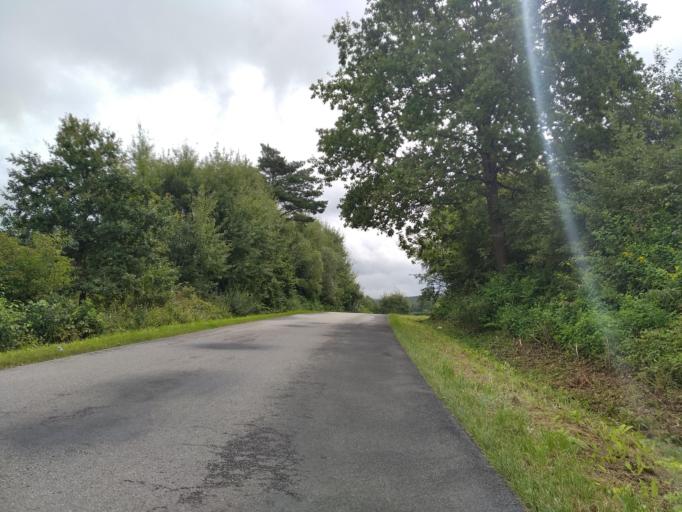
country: PL
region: Subcarpathian Voivodeship
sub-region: Powiat brzozowski
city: Nozdrzec
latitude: 49.7432
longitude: 22.2395
